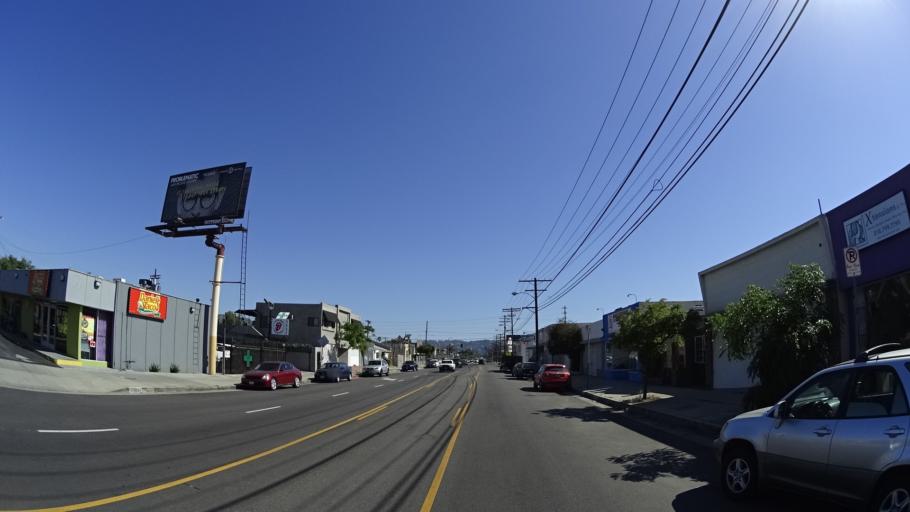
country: US
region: California
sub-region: Los Angeles County
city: North Hollywood
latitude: 34.1737
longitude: -118.3616
